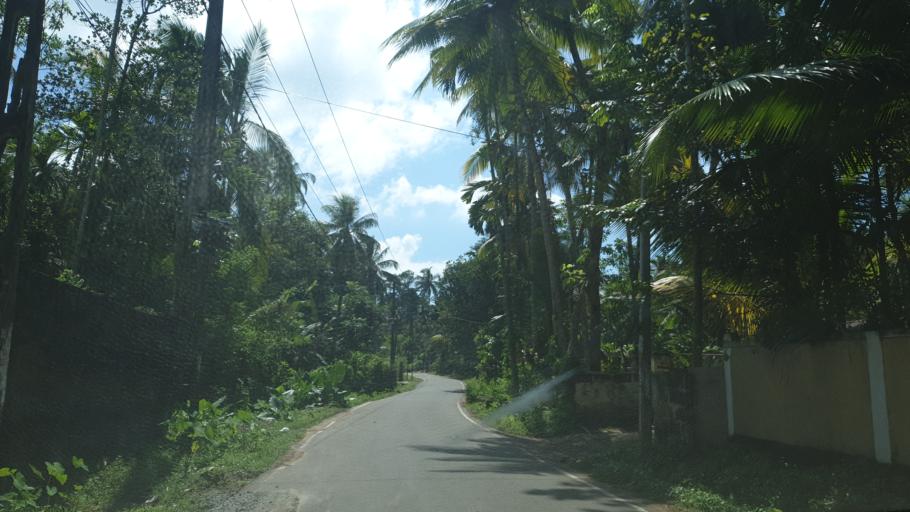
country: LK
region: Western
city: Panadura
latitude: 6.6793
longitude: 79.9299
